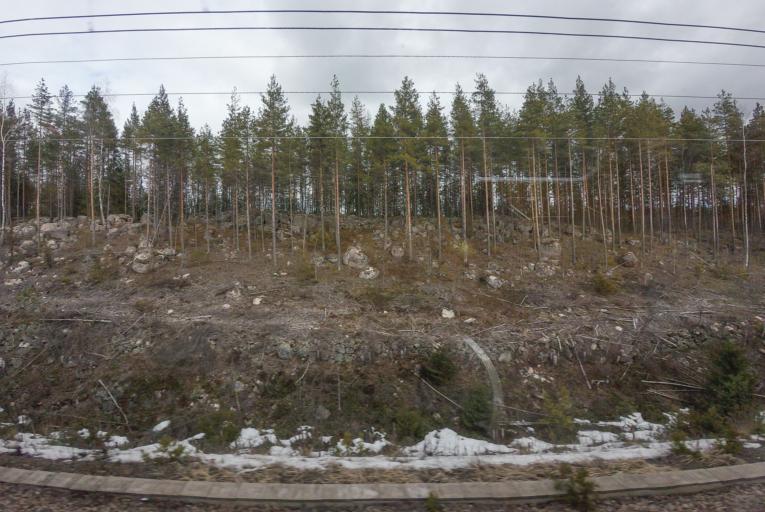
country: FI
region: Paijanne Tavastia
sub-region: Lahti
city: Artjaervi
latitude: 60.9226
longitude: 26.1455
